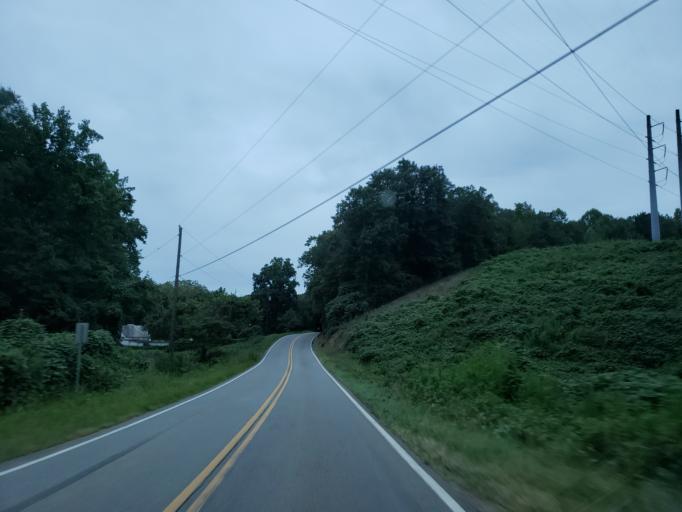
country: US
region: Georgia
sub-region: Cherokee County
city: Canton
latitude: 34.2786
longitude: -84.4501
